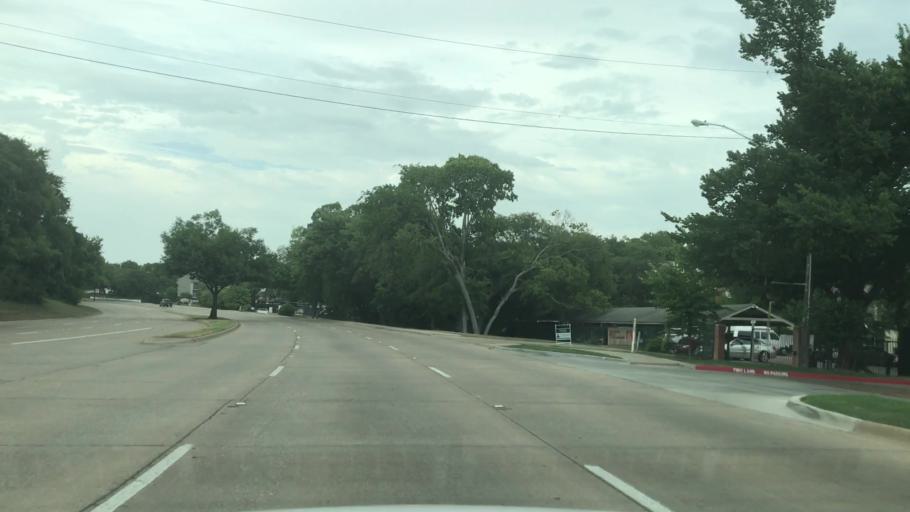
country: US
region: Texas
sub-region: Dallas County
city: Highland Park
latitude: 32.8700
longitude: -96.7356
